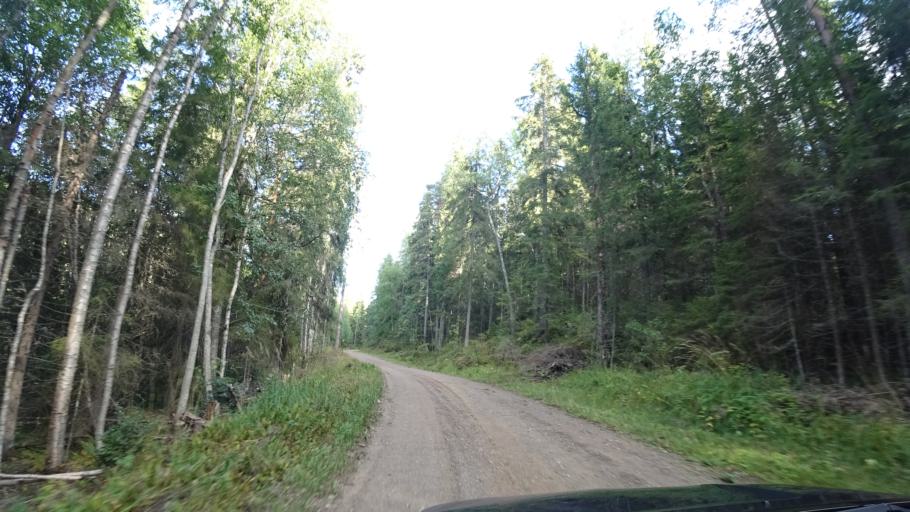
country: FI
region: Paijanne Tavastia
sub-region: Lahti
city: Auttoinen
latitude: 61.2218
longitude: 25.1995
